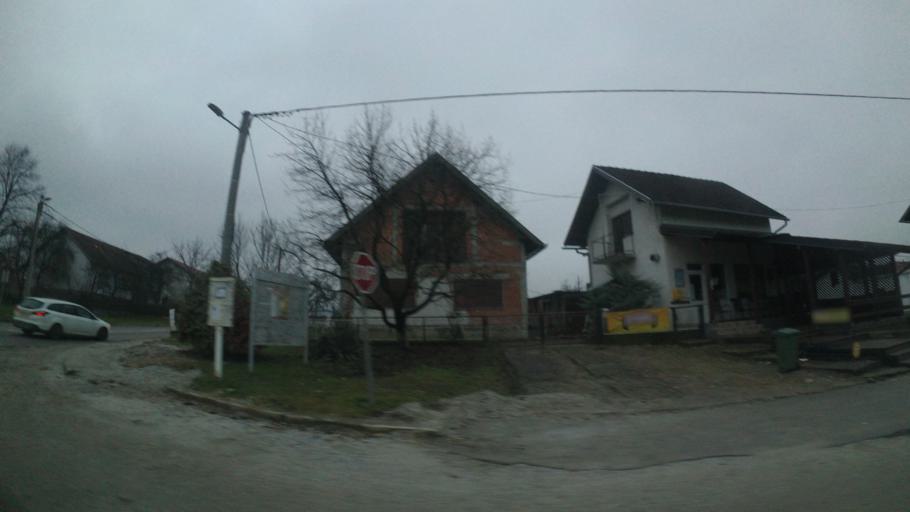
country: HR
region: Sisacko-Moslavacka
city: Petrinja
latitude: 45.4401
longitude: 16.2998
